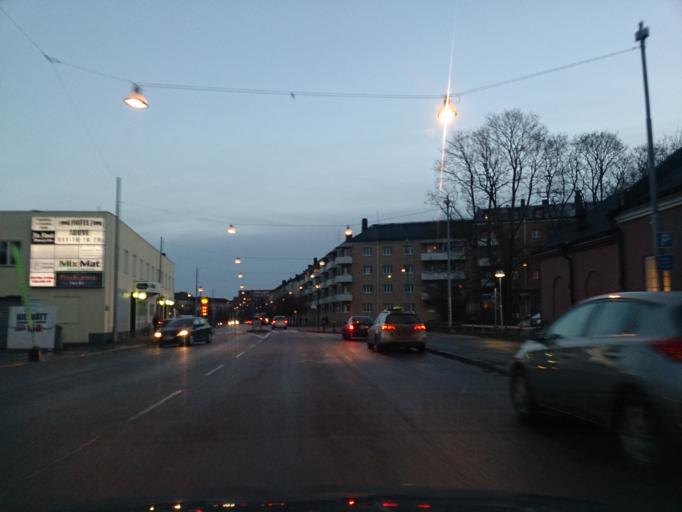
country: SE
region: OEstergoetland
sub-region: Norrkopings Kommun
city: Norrkoping
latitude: 58.5971
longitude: 16.1712
